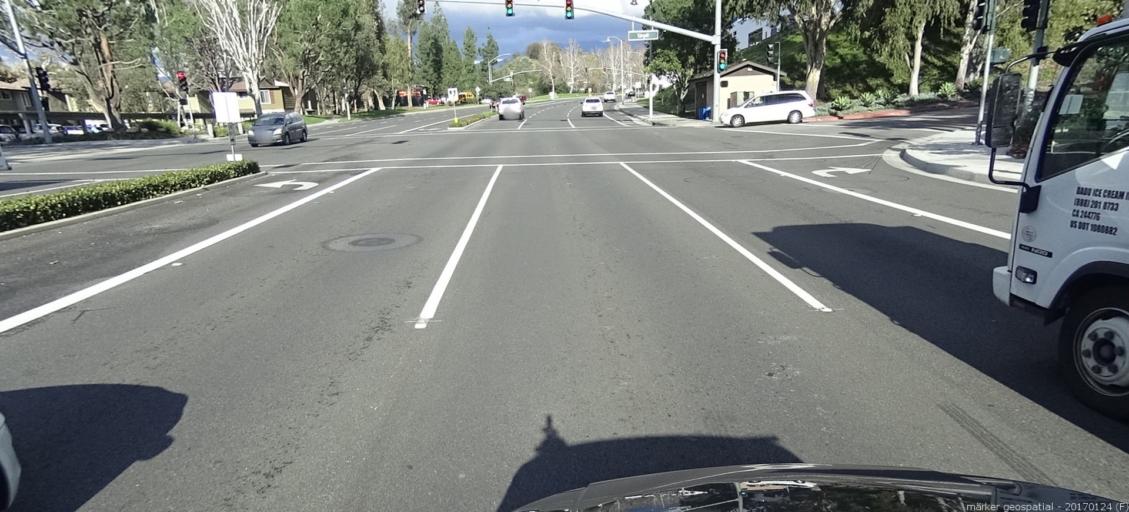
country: US
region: California
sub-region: Orange County
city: Lake Forest
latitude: 33.6252
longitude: -117.6825
